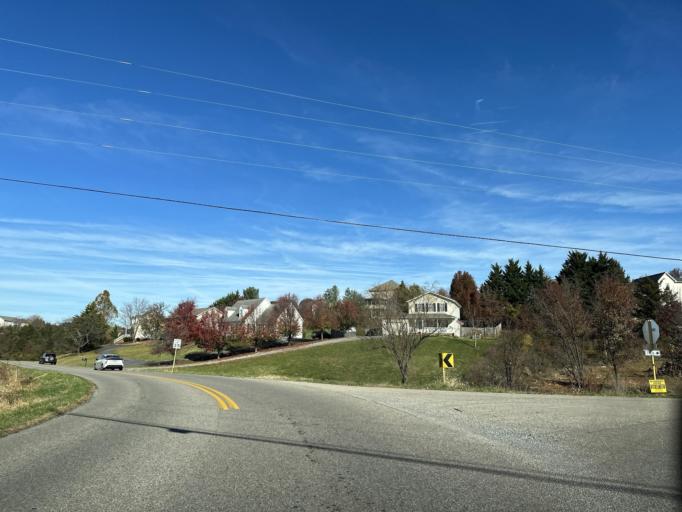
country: US
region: Virginia
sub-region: Augusta County
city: Fishersville
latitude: 38.1043
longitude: -78.9623
